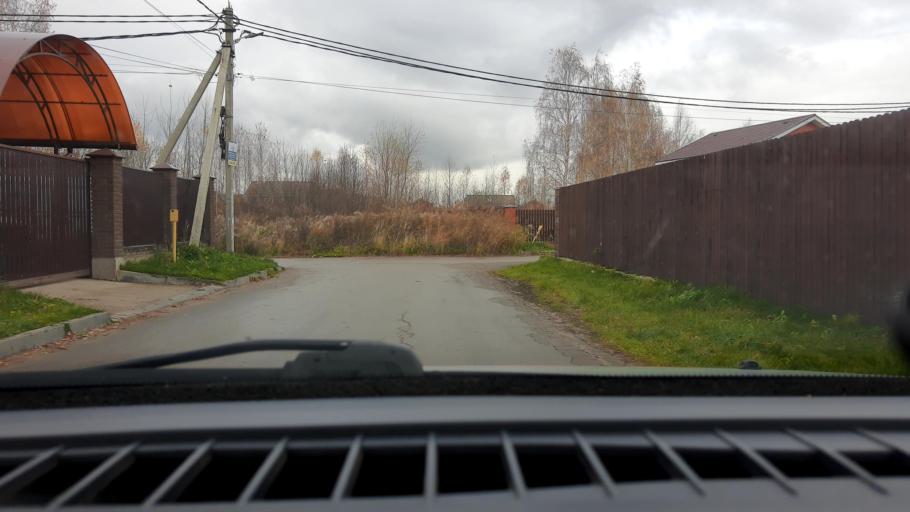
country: RU
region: Nizjnij Novgorod
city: Afonino
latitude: 56.2043
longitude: 44.1241
